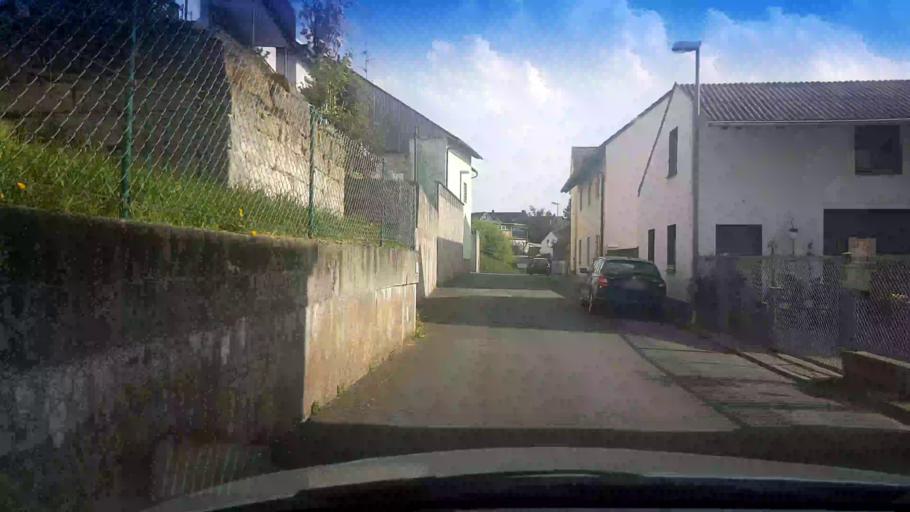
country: DE
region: Bavaria
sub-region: Upper Franconia
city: Rattelsdorf
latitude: 50.0151
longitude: 10.8838
